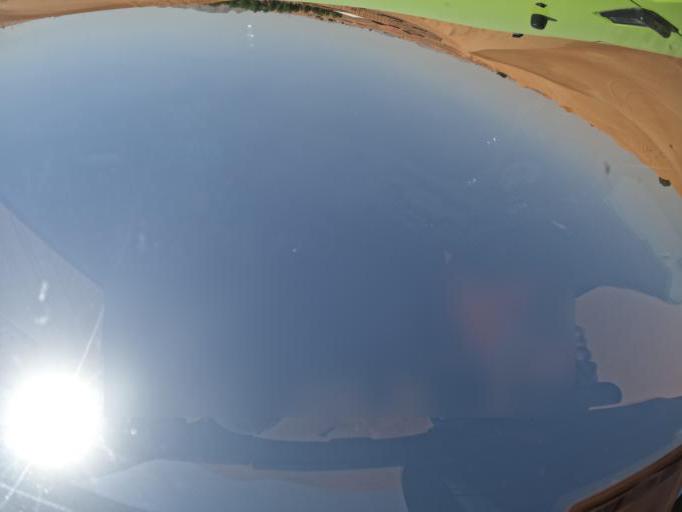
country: AE
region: Ash Shariqah
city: Adh Dhayd
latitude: 25.0103
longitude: 55.7358
